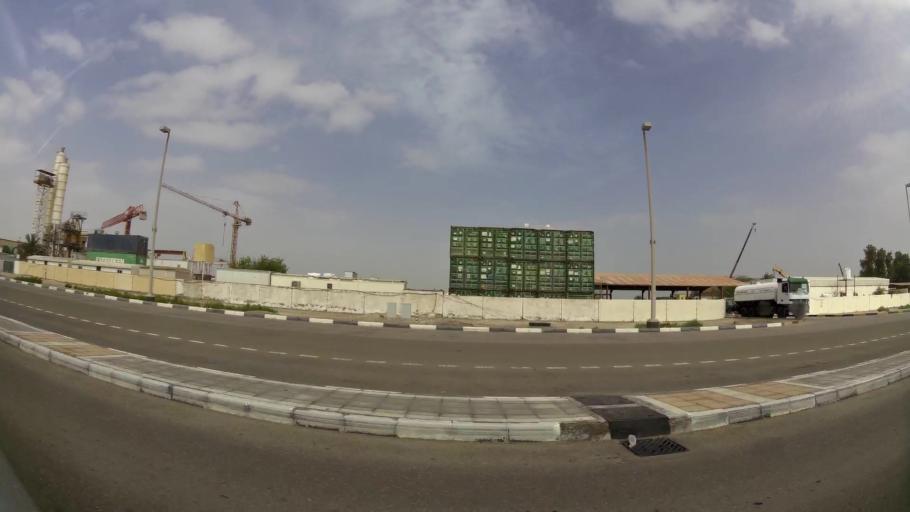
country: AE
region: Abu Dhabi
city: Abu Dhabi
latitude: 24.3807
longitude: 54.4738
